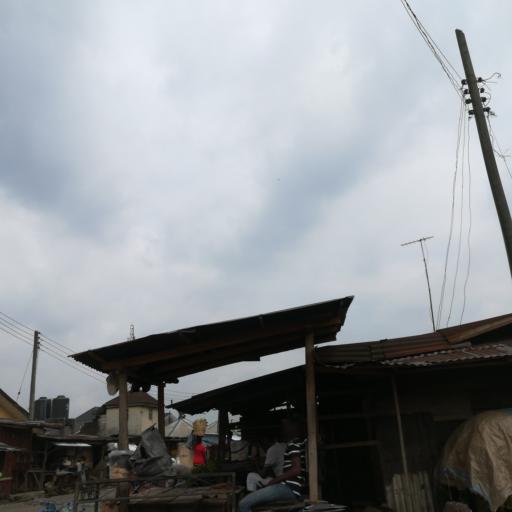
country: NG
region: Rivers
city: Port Harcourt
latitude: 4.8402
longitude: 7.0735
